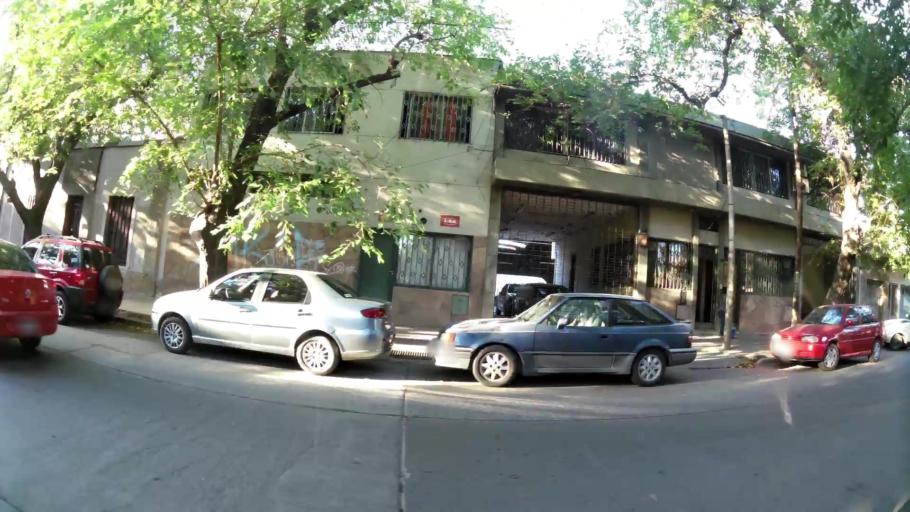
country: AR
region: Mendoza
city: Mendoza
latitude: -32.8796
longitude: -68.8424
